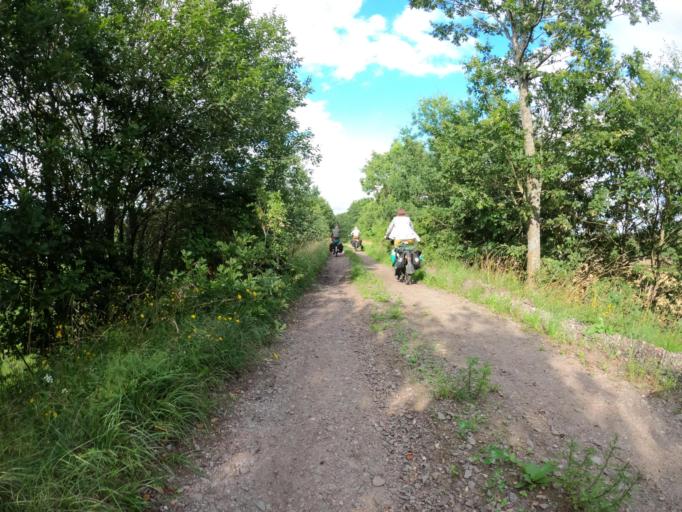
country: PL
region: West Pomeranian Voivodeship
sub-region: Powiat szczecinecki
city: Grzmiaca
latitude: 53.8730
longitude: 16.4635
